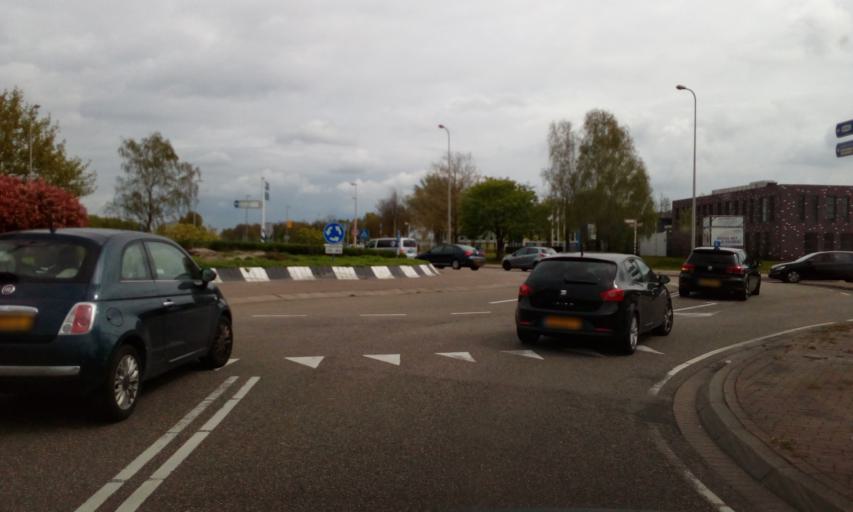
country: NL
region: South Holland
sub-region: Gemeente Barendrecht
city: Barendrecht
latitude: 51.8626
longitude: 4.5361
